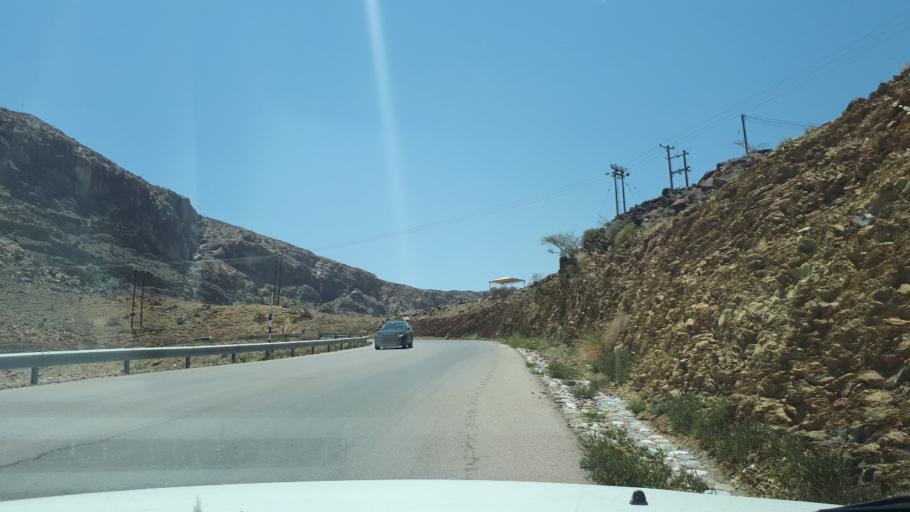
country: OM
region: Muhafazat ad Dakhiliyah
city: Bahla'
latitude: 23.2249
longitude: 57.1438
